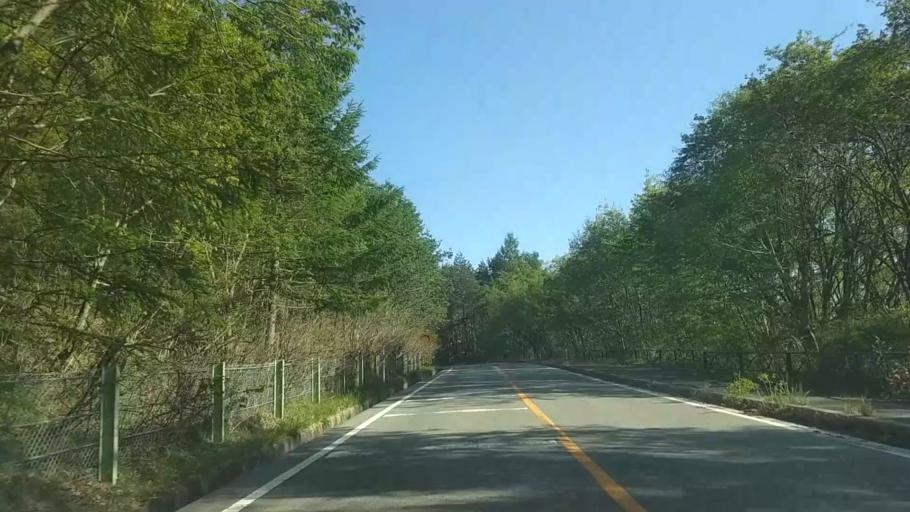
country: JP
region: Yamanashi
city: Nirasaki
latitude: 35.8998
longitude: 138.3599
